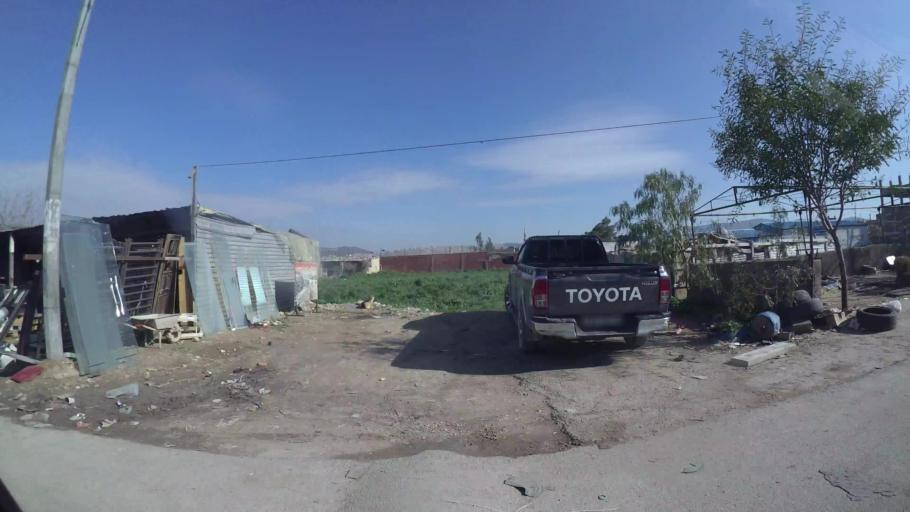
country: JO
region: Amman
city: Al Jubayhah
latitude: 32.0797
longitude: 35.8513
